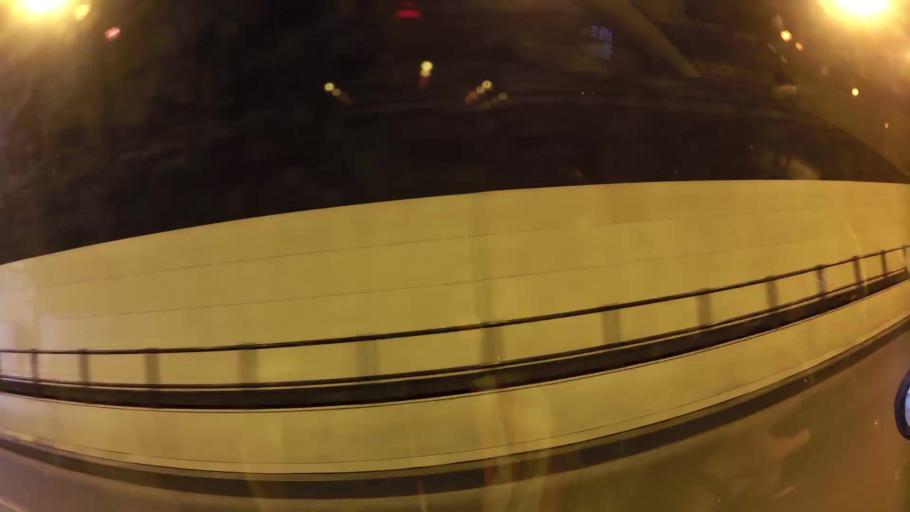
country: EC
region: Pichincha
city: Quito
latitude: -0.2185
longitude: -78.5199
